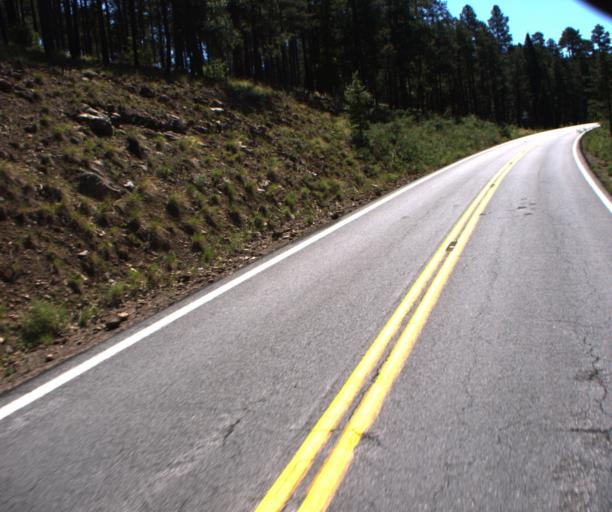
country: US
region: Arizona
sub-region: Apache County
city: Eagar
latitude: 33.7337
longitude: -109.2049
